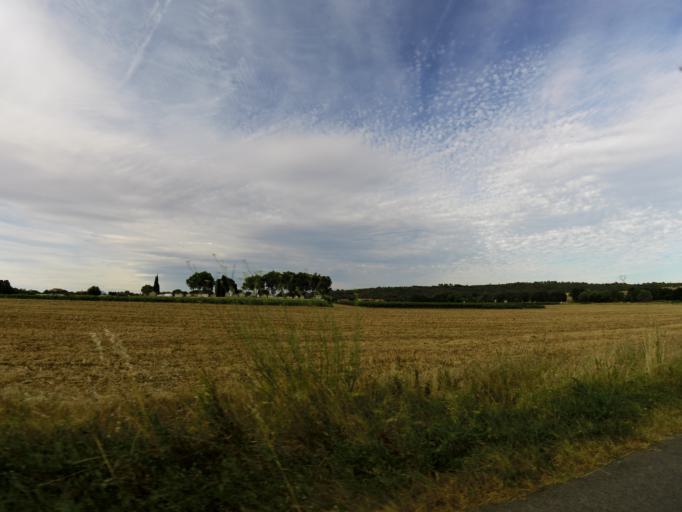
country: FR
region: Languedoc-Roussillon
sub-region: Departement du Gard
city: Saint-Mamert-du-Gard
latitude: 43.8822
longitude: 4.1905
